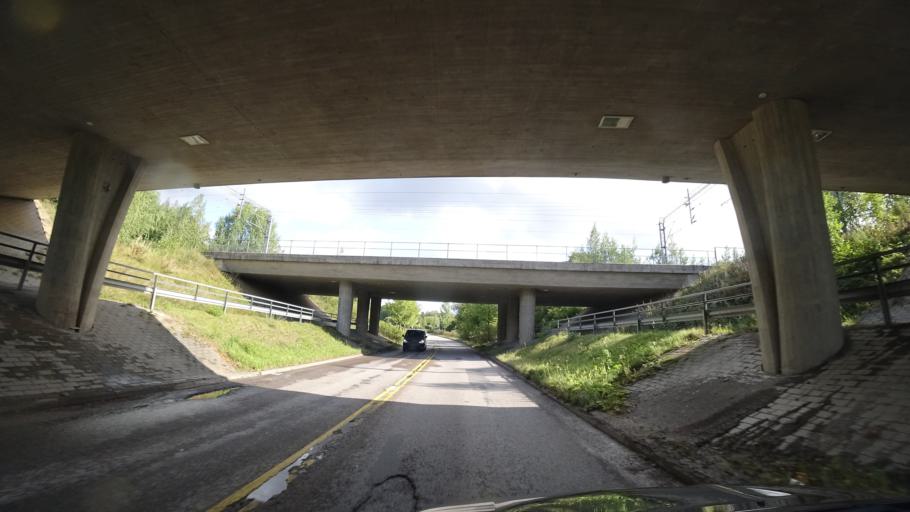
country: FI
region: Uusimaa
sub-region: Helsinki
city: Hyvinge
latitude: 60.5542
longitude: 24.9670
